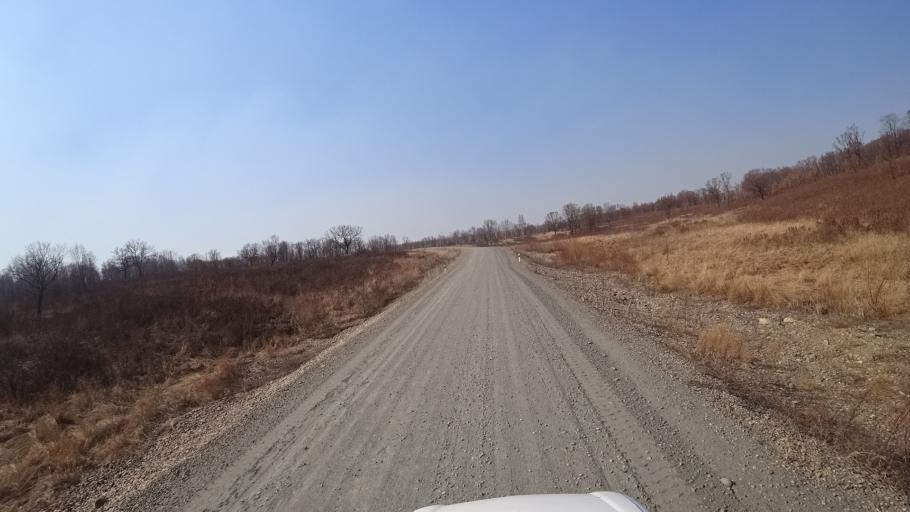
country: RU
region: Amur
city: Novobureyskiy
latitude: 49.8245
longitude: 129.9959
